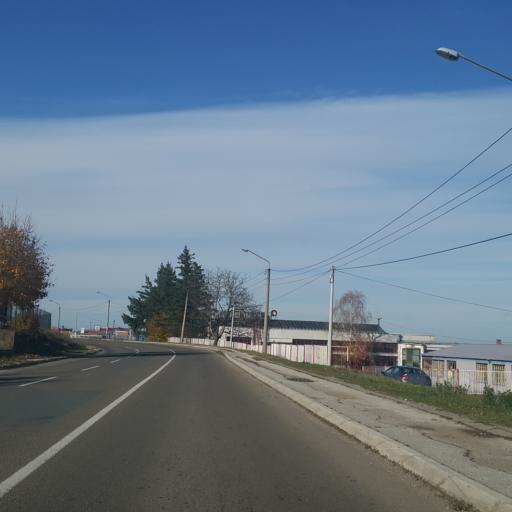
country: RS
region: Central Serbia
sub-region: Sumadijski Okrug
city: Topola
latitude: 44.2528
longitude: 20.6884
